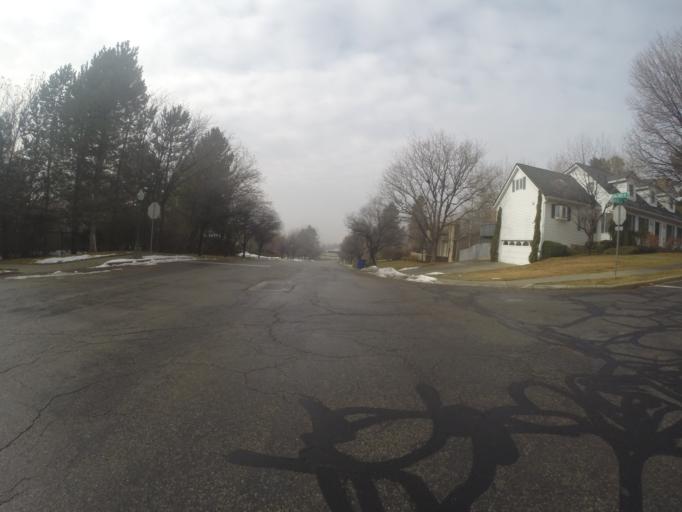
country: US
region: Utah
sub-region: Salt Lake County
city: Salt Lake City
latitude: 40.7748
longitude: -111.8498
